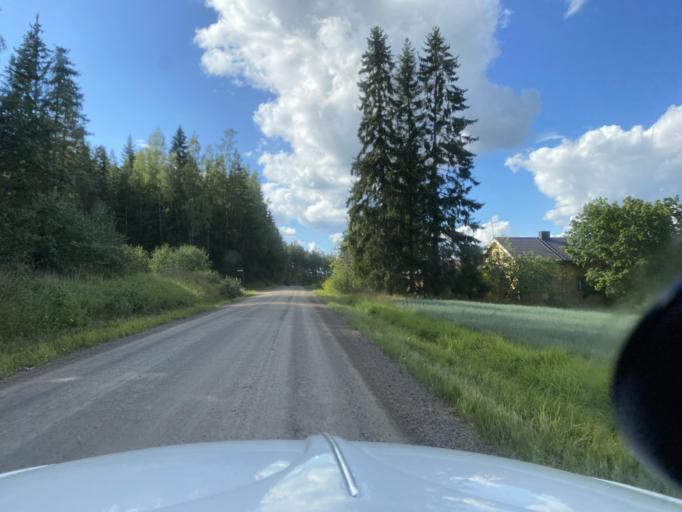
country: FI
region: Pirkanmaa
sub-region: Lounais-Pirkanmaa
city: Punkalaidun
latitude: 61.1234
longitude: 23.2622
